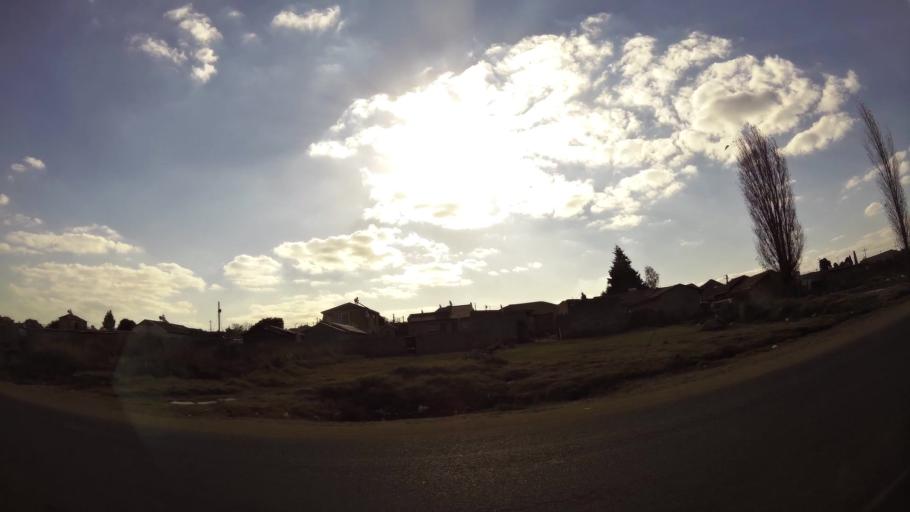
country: ZA
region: Gauteng
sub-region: Ekurhuleni Metropolitan Municipality
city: Tembisa
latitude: -26.0000
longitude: 28.1838
